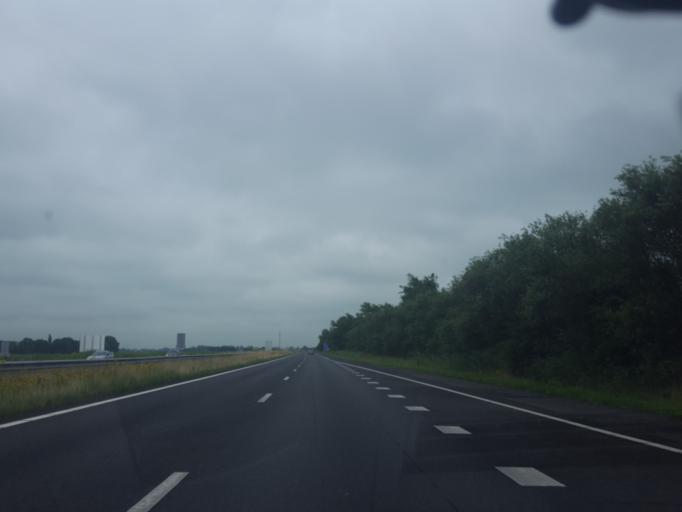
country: NL
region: Friesland
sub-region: Gemeente Leeuwarden
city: Wirdum
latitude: 53.1406
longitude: 5.7979
